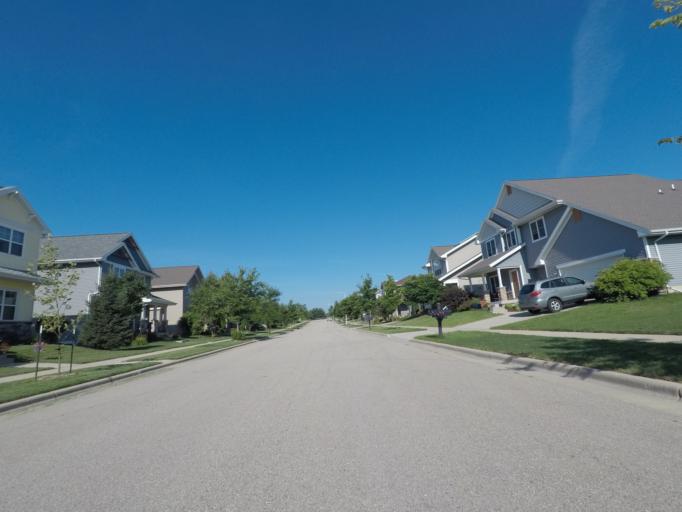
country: US
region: Wisconsin
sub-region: Dane County
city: Middleton
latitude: 43.0666
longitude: -89.5491
